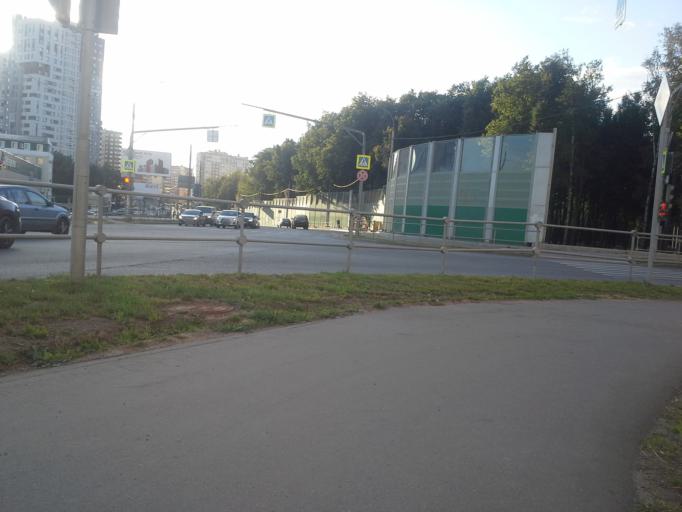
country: RU
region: Moskovskaya
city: Kommunarka
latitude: 55.5664
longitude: 37.4851
